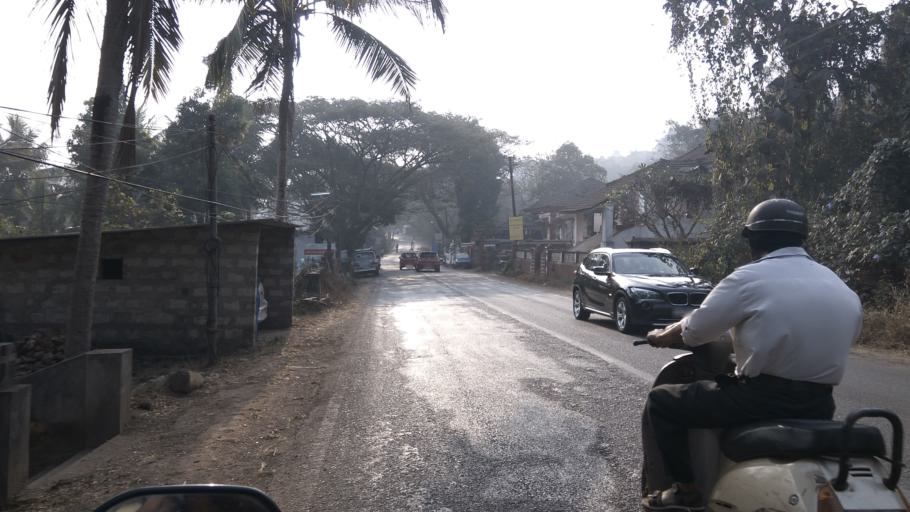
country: IN
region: Goa
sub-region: North Goa
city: Saligao
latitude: 15.5445
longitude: 73.8064
